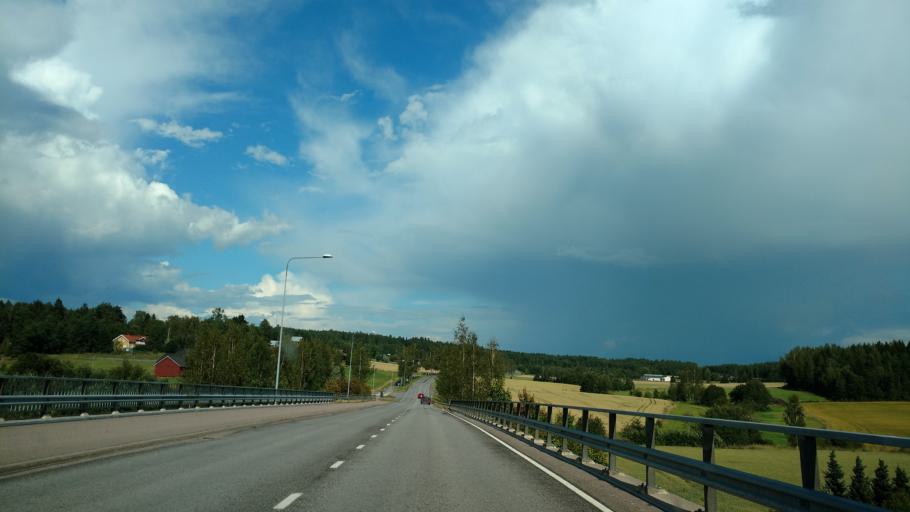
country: FI
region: Varsinais-Suomi
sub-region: Turku
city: Paimio
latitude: 60.4531
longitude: 22.7060
